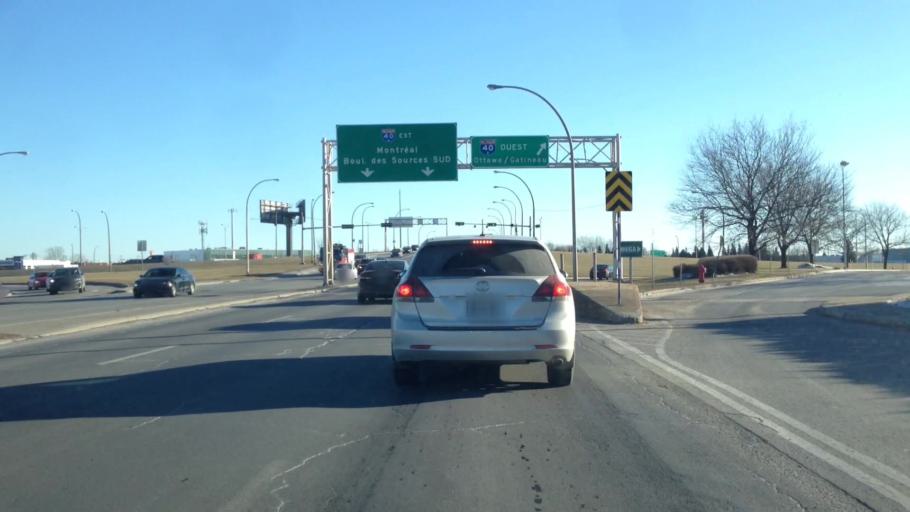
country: CA
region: Quebec
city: Dollard-Des Ormeaux
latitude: 45.4822
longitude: -73.7952
